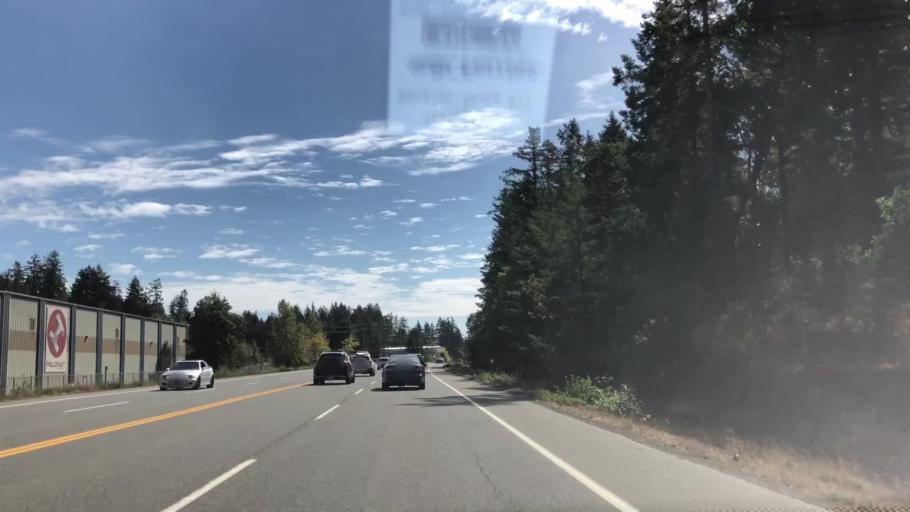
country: CA
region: British Columbia
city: Nanaimo
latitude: 49.1351
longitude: -123.8726
